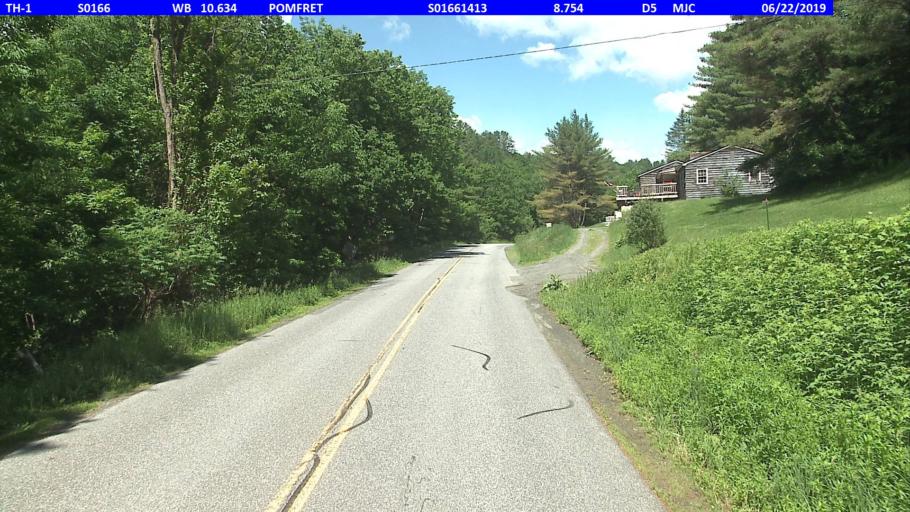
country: US
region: Vermont
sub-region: Windsor County
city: Woodstock
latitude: 43.7182
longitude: -72.4335
